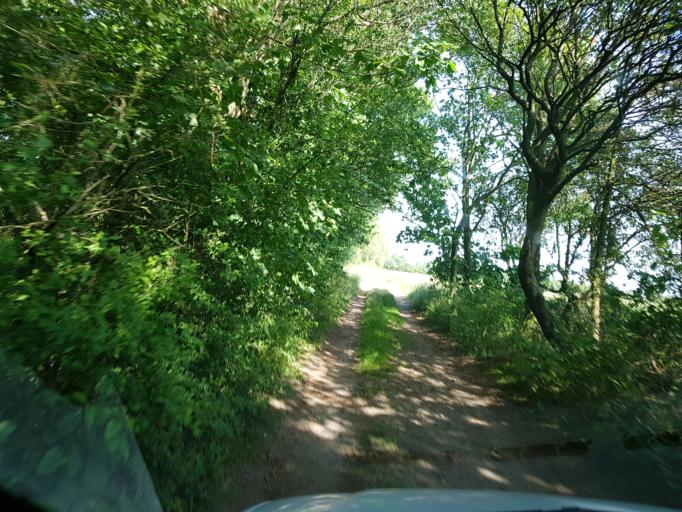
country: DK
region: South Denmark
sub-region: Esbjerg Kommune
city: Ribe
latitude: 55.3890
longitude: 8.7358
